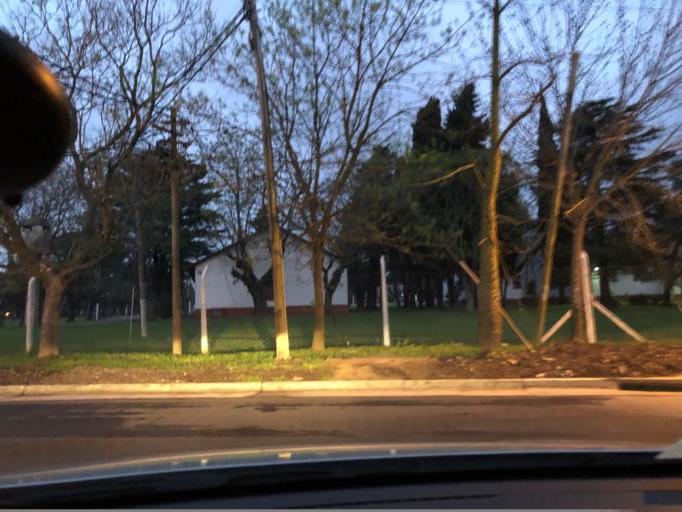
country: AR
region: Buenos Aires
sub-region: Partido de La Plata
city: La Plata
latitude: -34.8707
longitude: -58.0403
